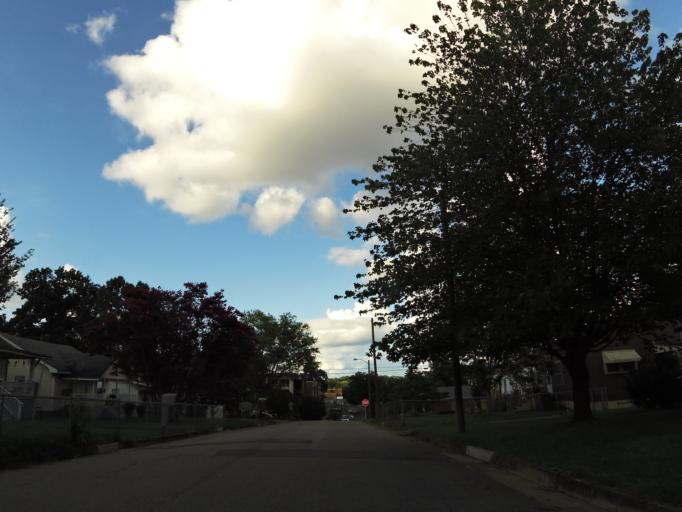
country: US
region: Tennessee
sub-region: Knox County
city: Knoxville
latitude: 35.9897
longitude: -83.9277
